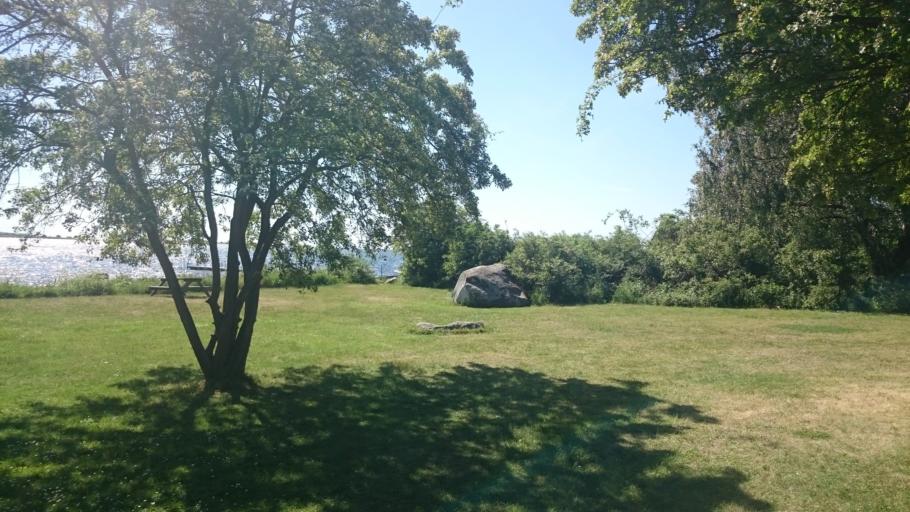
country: SE
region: Blekinge
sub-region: Solvesborgs Kommun
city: Soelvesborg
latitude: 56.0395
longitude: 14.5213
